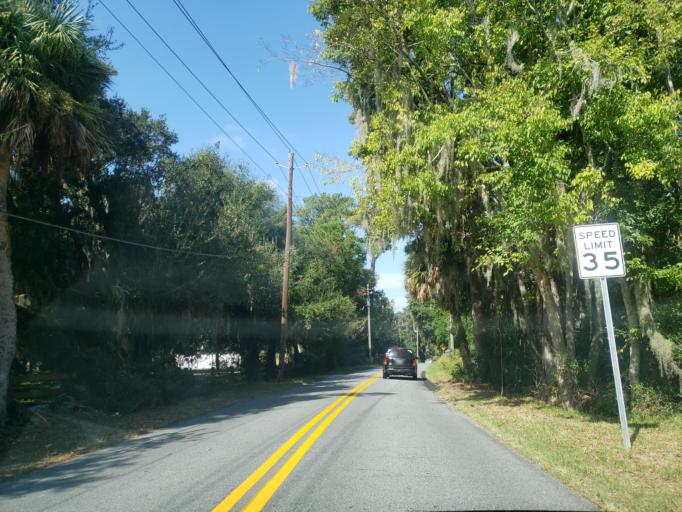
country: US
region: Georgia
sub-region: Chatham County
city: Montgomery
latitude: 31.9375
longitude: -81.1047
